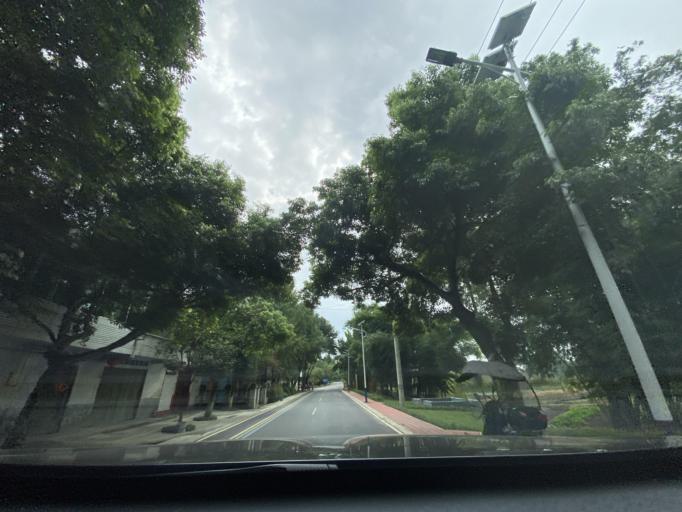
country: CN
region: Sichuan
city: Wujin
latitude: 30.4005
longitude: 103.9871
